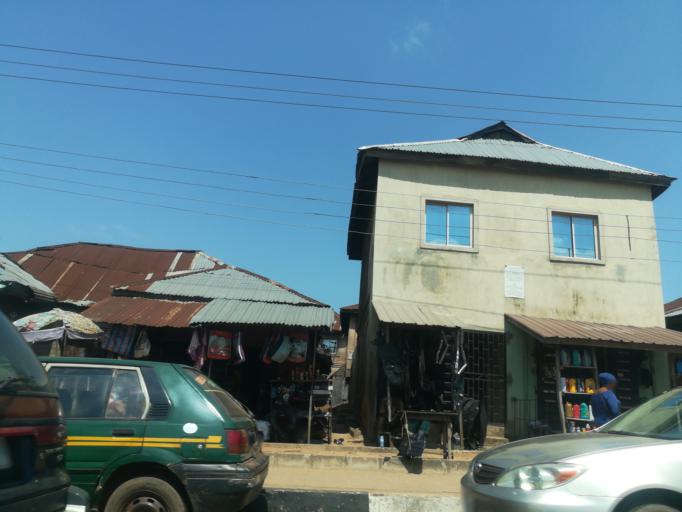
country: NG
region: Ogun
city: Abeokuta
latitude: 7.1529
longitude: 3.3499
